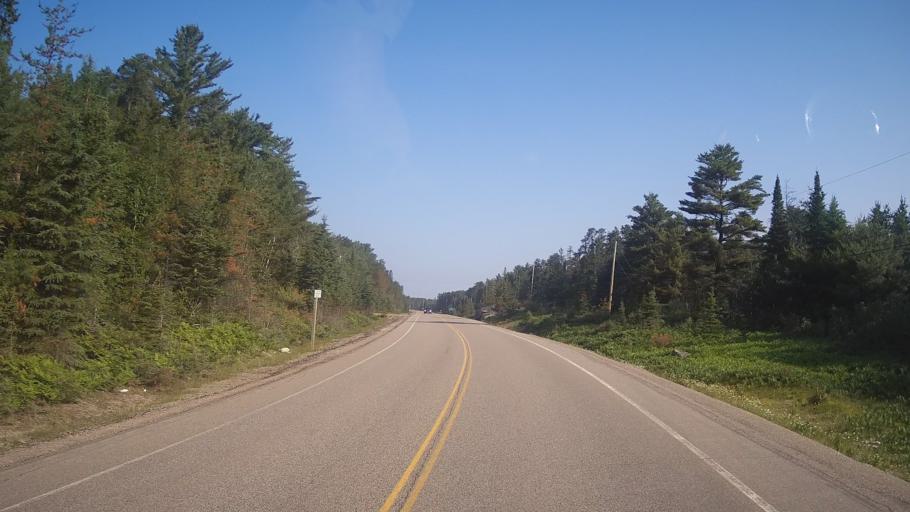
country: CA
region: Ontario
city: Rayside-Balfour
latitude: 46.7131
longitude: -81.5622
